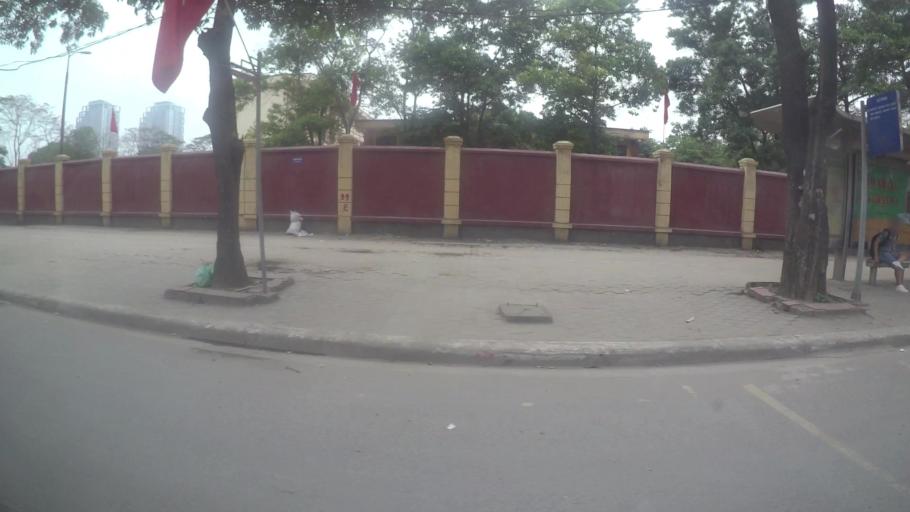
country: VN
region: Ha Noi
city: Cau Dien
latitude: 21.0126
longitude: 105.7705
